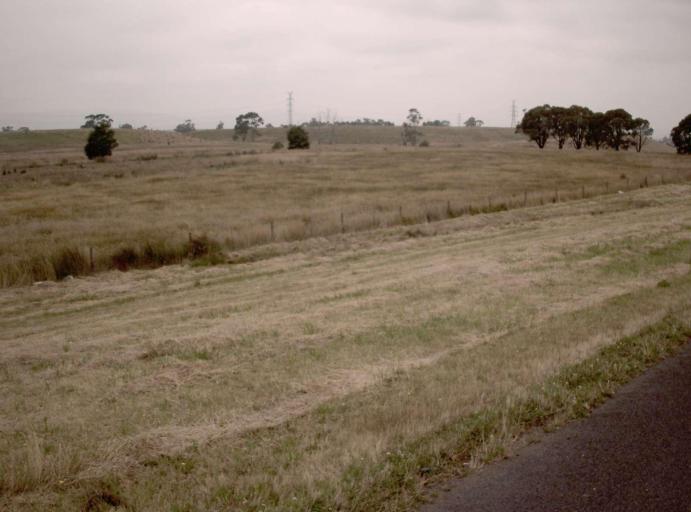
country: AU
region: Victoria
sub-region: Latrobe
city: Morwell
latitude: -38.2500
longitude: 146.3328
